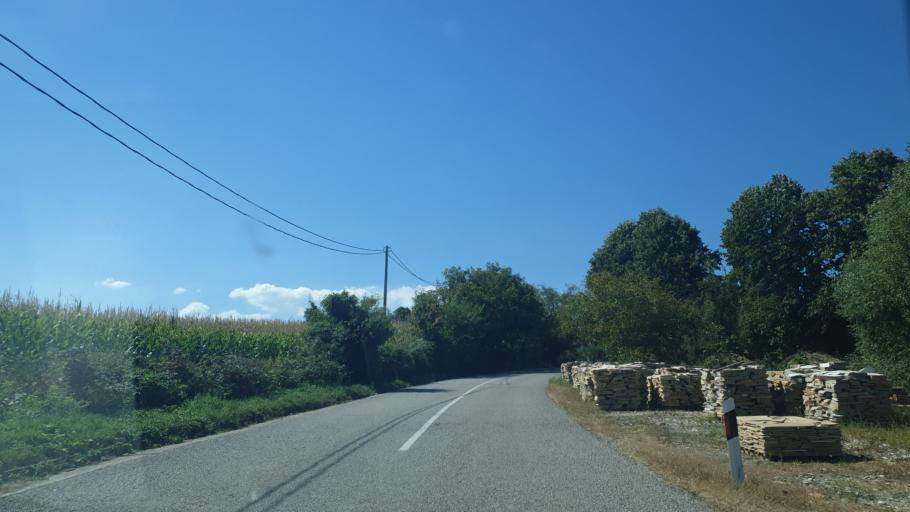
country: RS
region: Central Serbia
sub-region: Kolubarski Okrug
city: Mionica
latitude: 44.1864
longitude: 20.0631
